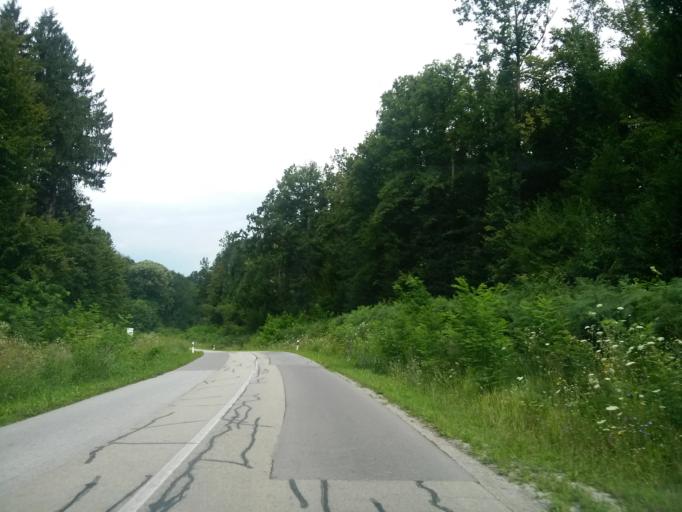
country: HR
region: Sisacko-Moslavacka
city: Gvozd
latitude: 45.3115
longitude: 15.9683
